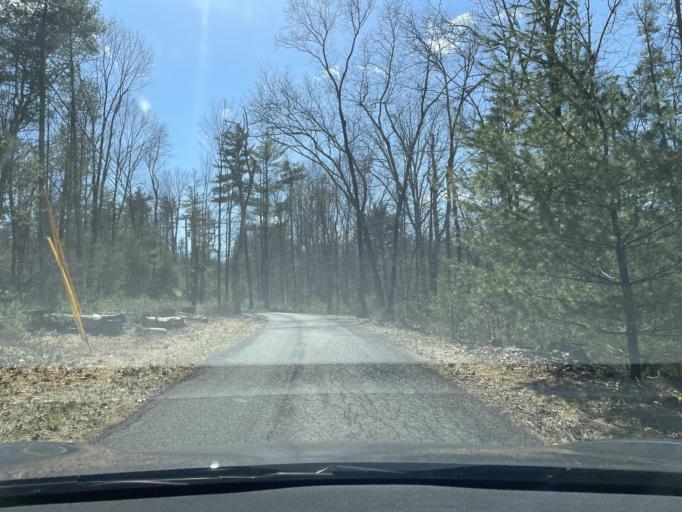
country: US
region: New York
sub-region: Ulster County
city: West Hurley
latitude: 41.9542
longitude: -74.1110
